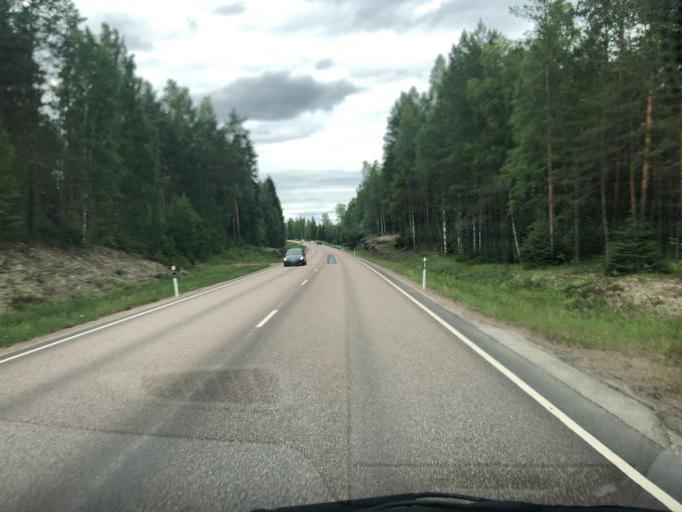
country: FI
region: Southern Savonia
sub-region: Mikkeli
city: Maentyharju
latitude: 61.1239
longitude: 27.1015
